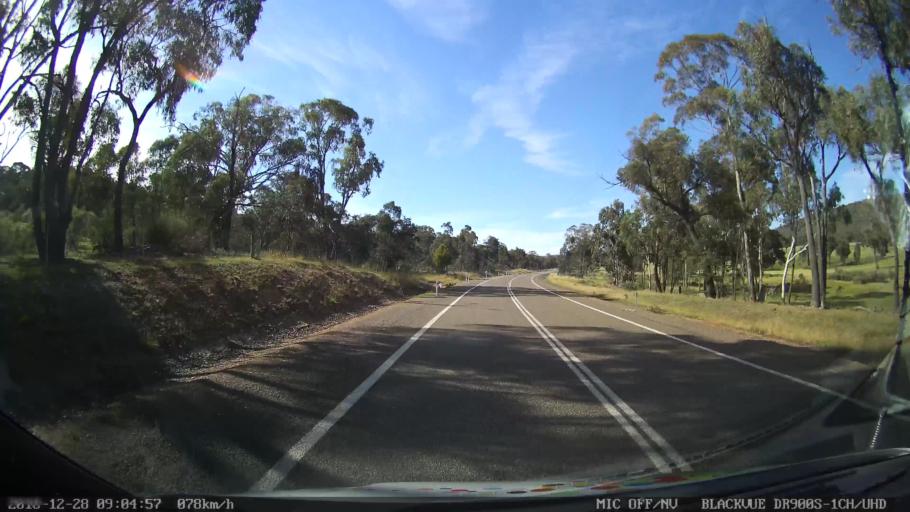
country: AU
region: New South Wales
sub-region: Upper Lachlan Shire
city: Crookwell
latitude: -34.1783
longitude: 149.3475
